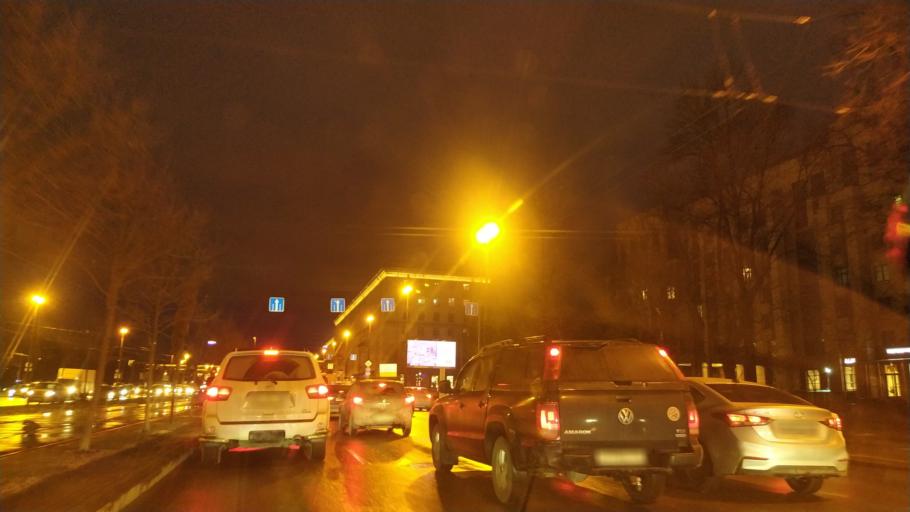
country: RU
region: St.-Petersburg
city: Kupchino
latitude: 59.8561
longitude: 30.3215
